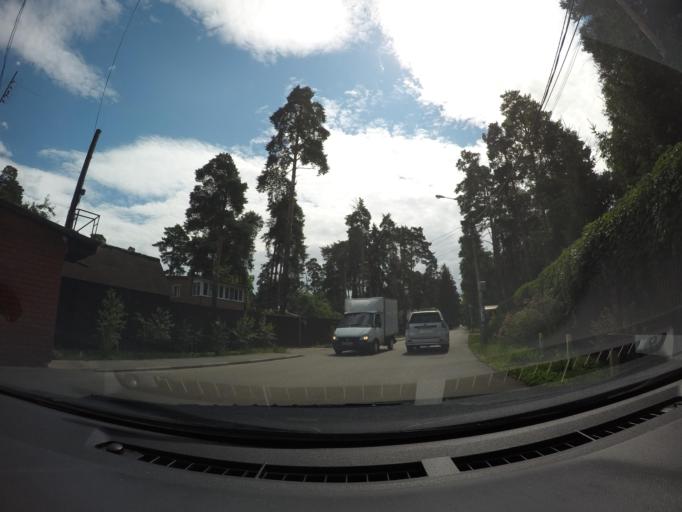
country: RU
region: Moskovskaya
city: Malakhovka
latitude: 55.6461
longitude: 38.0394
